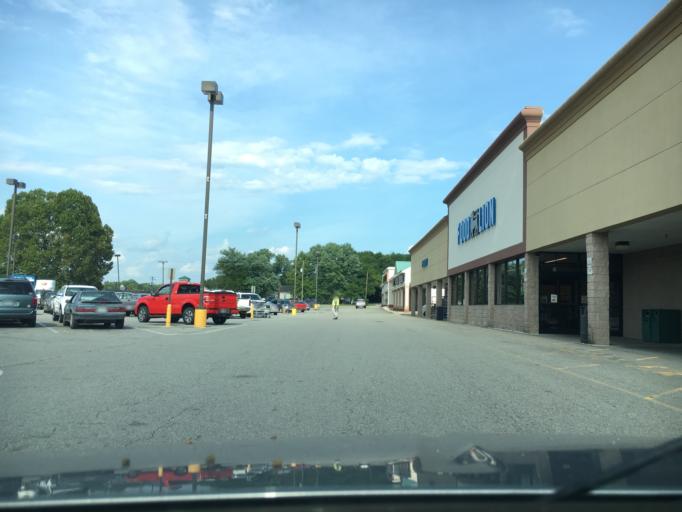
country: US
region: Virginia
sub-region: Halifax County
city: South Boston
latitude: 36.6864
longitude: -78.8976
